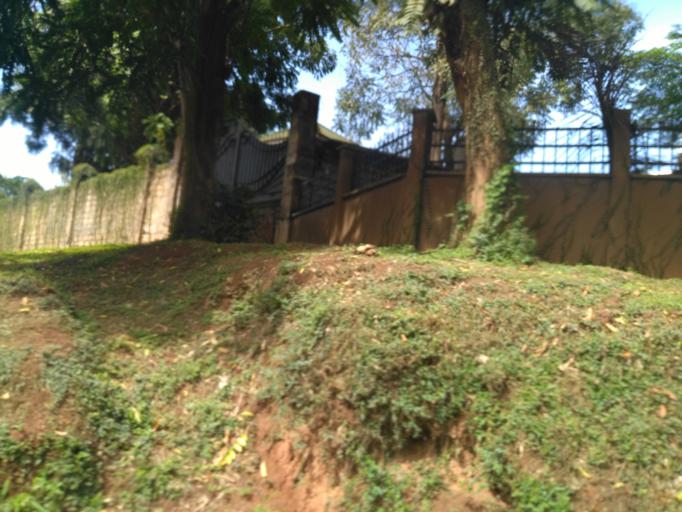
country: UG
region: Central Region
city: Kampala Central Division
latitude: 0.3230
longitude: 32.5802
